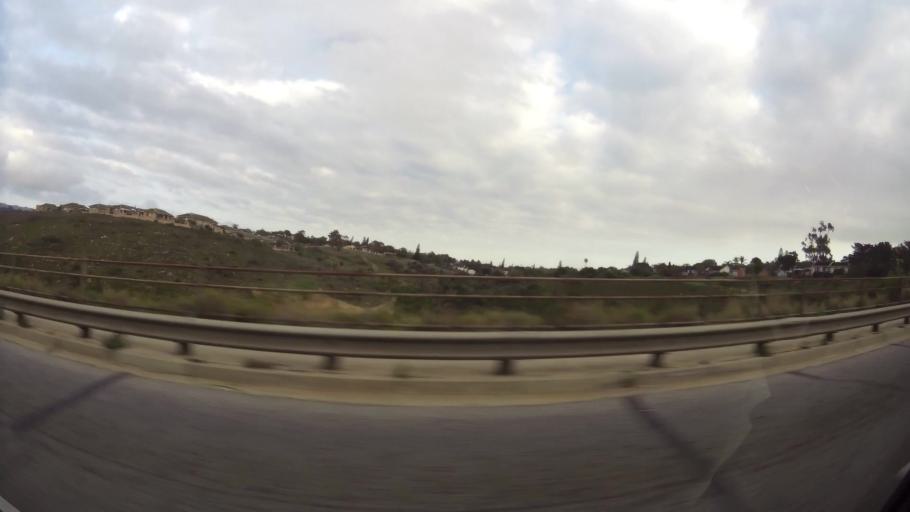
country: ZA
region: Eastern Cape
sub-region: Nelson Mandela Bay Metropolitan Municipality
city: Port Elizabeth
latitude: -33.9506
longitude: 25.5543
